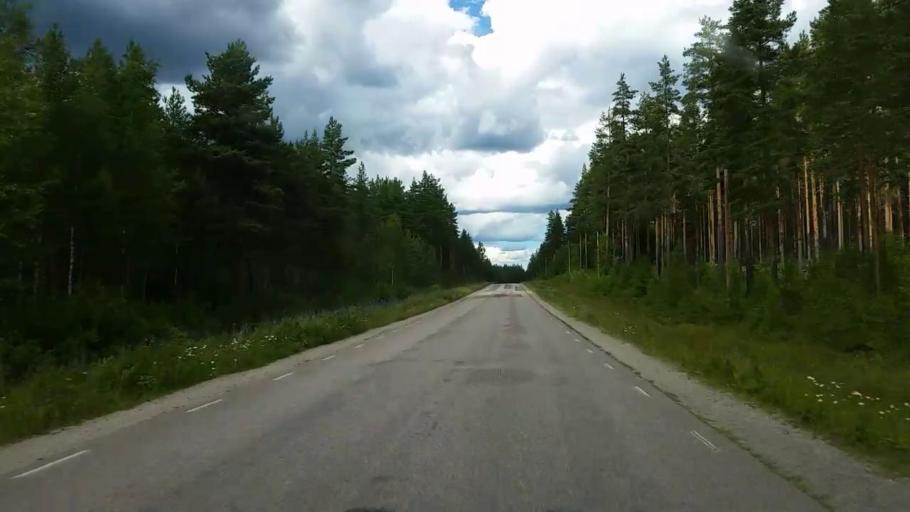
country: SE
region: Gaevleborg
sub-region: Ovanakers Kommun
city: Edsbyn
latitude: 61.4046
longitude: 15.8964
